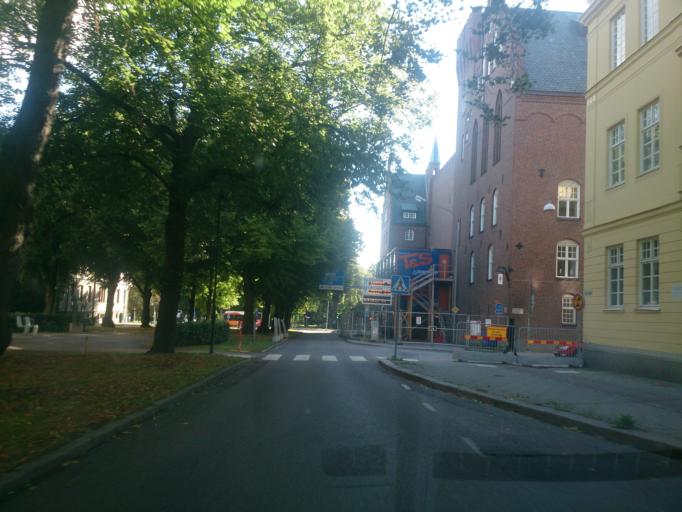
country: SE
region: OEstergoetland
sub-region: Linkopings Kommun
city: Linkoping
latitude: 58.4144
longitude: 15.6212
